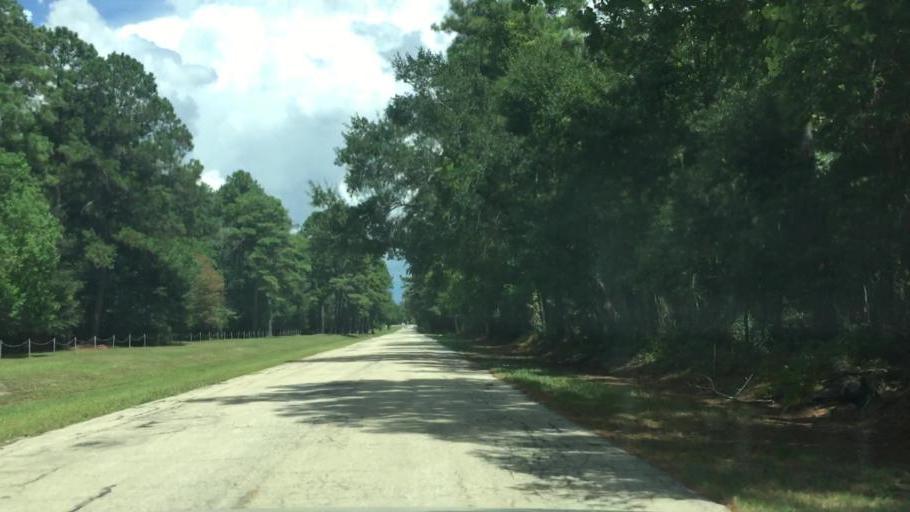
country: US
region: Texas
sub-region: Harris County
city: Jersey Village
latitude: 29.8132
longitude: -95.6241
